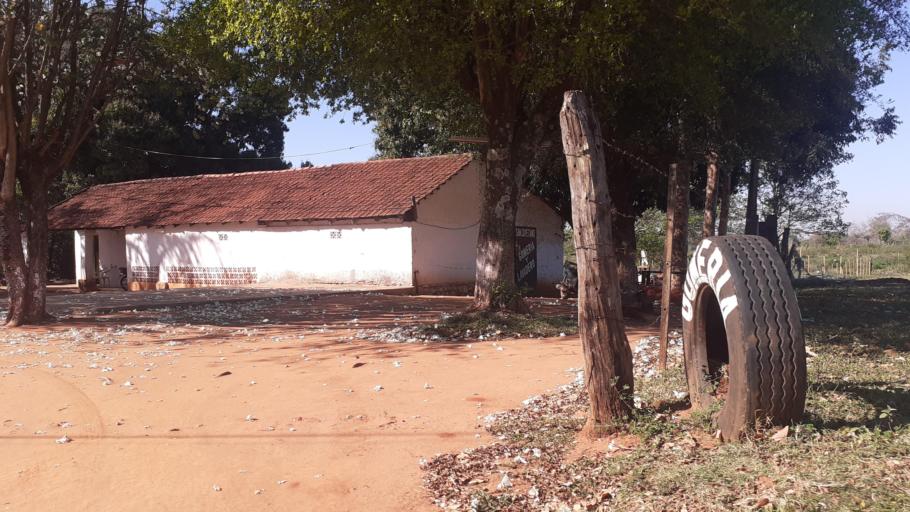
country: PY
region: Misiones
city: San Juan Bautista
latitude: -26.6676
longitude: -57.1265
